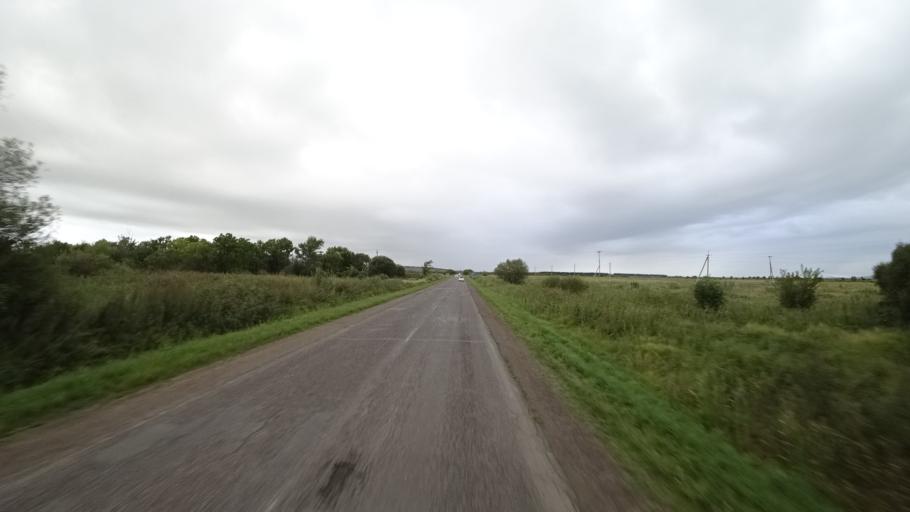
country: RU
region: Primorskiy
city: Chernigovka
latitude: 44.3554
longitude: 132.5634
